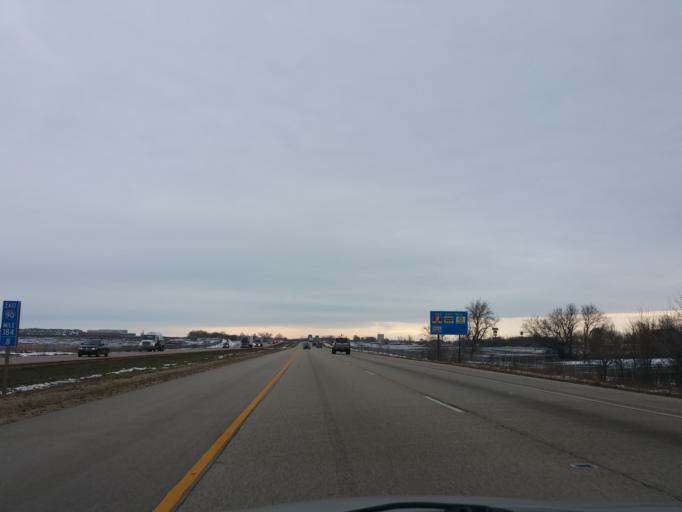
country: US
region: Wisconsin
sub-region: Rock County
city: Beloit
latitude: 42.5373
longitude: -88.9752
